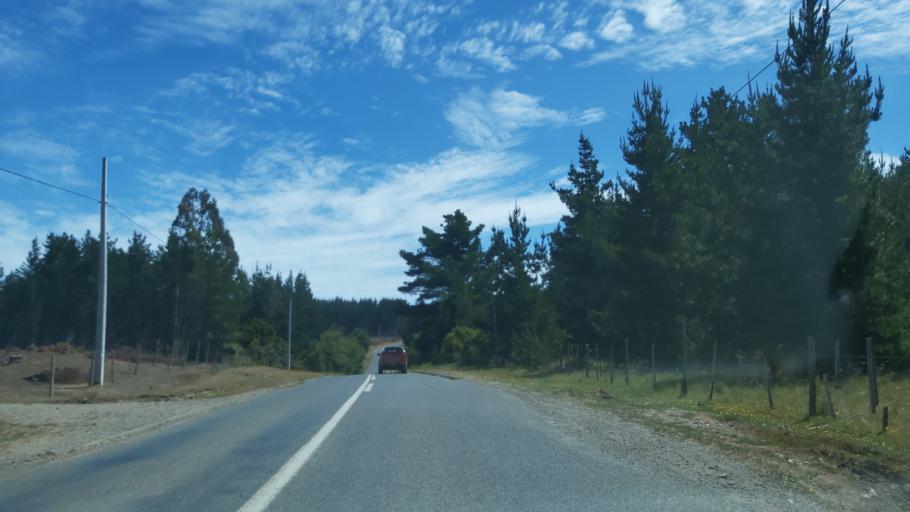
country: CL
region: Maule
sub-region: Provincia de Talca
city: Constitucion
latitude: -35.5477
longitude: -72.5646
